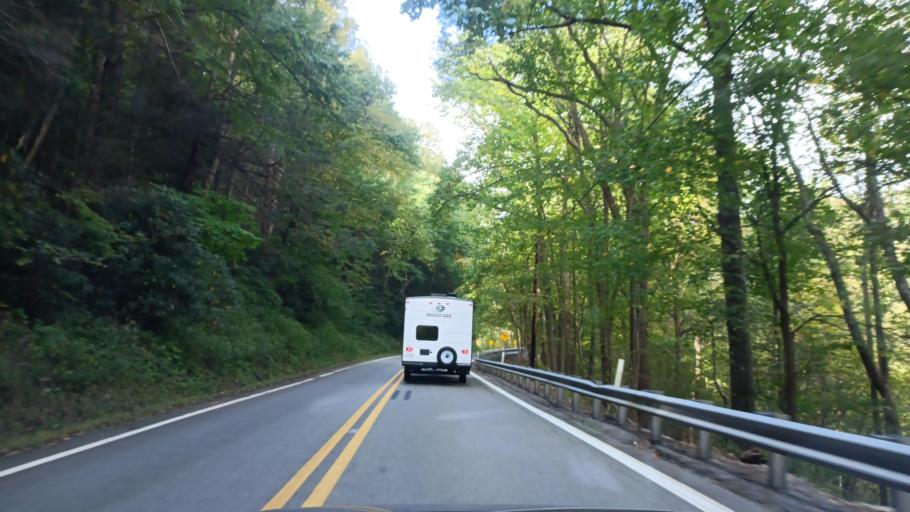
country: US
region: West Virginia
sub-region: Preston County
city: Terra Alta
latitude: 39.2960
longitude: -79.6209
